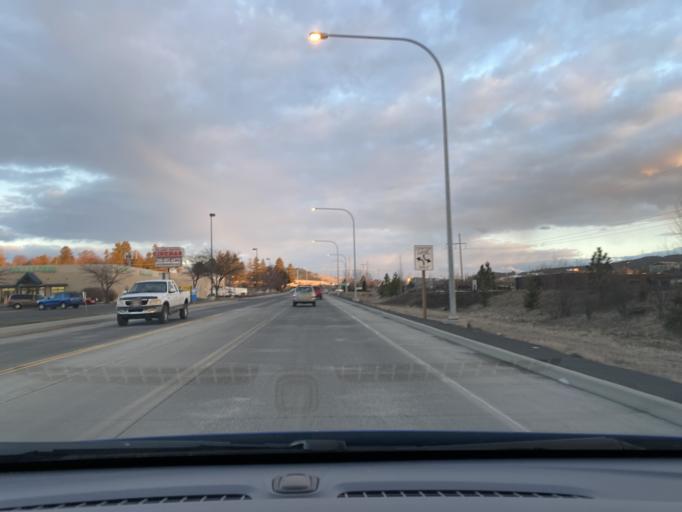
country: US
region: Idaho
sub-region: Latah County
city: Moscow
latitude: 46.7209
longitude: -116.9850
